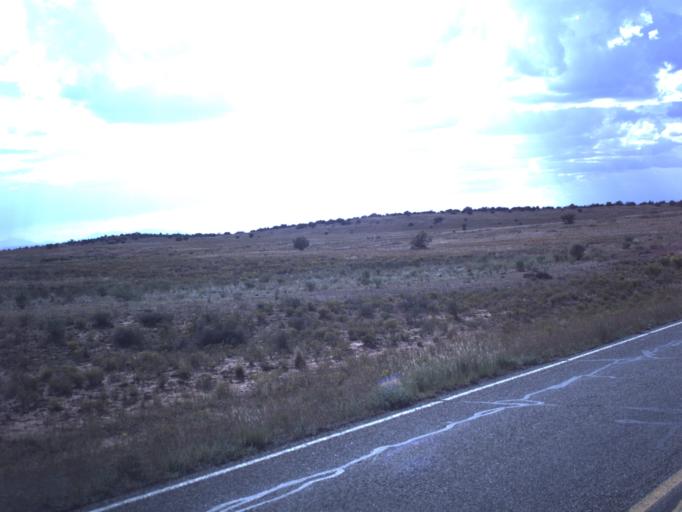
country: US
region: Utah
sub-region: Grand County
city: Moab
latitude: 38.5511
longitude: -109.7846
